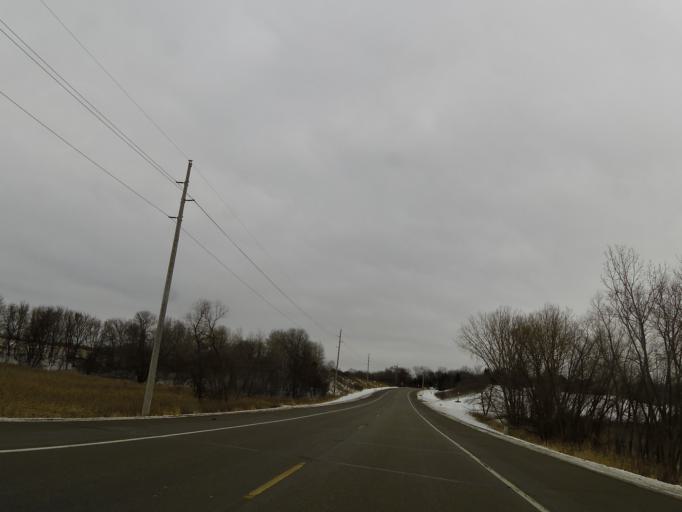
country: US
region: Minnesota
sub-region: Dakota County
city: Rosemount
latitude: 44.7681
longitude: -93.1276
